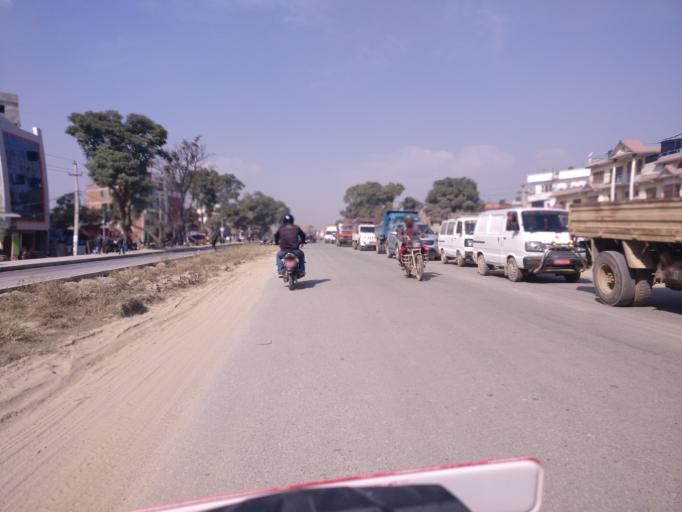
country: NP
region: Central Region
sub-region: Bagmati Zone
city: Patan
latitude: 27.6618
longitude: 85.3178
